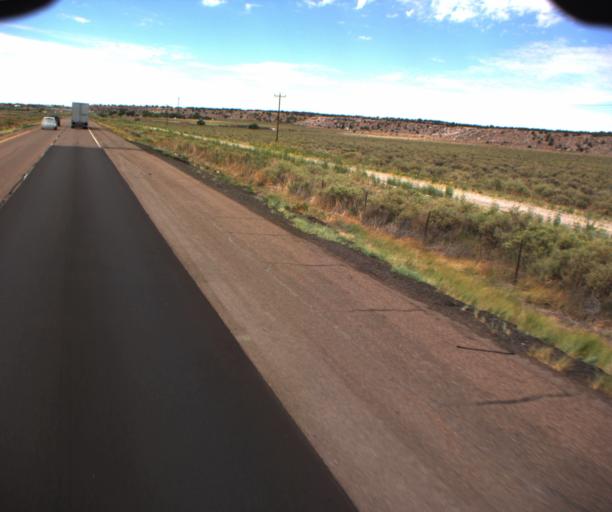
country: US
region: Arizona
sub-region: Apache County
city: Houck
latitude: 35.1723
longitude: -109.4745
